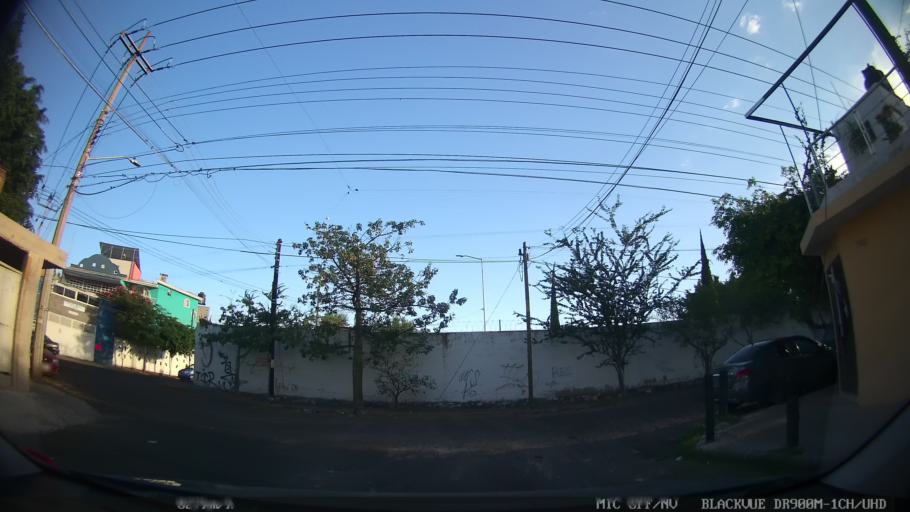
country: MX
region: Jalisco
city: Tlaquepaque
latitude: 20.7056
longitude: -103.2973
